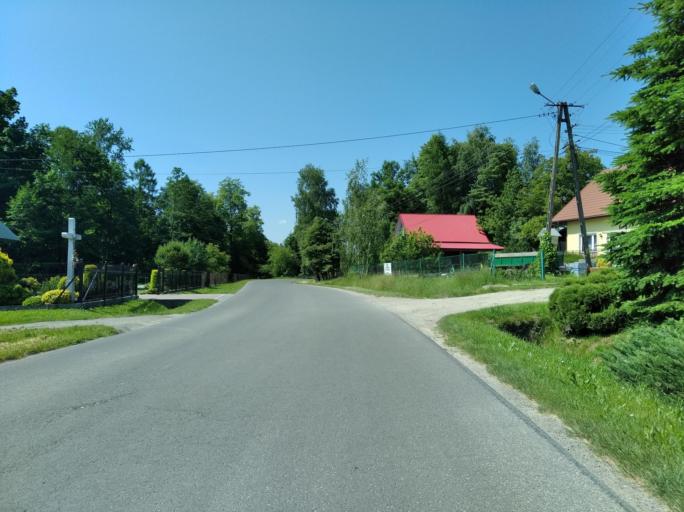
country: PL
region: Subcarpathian Voivodeship
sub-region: Powiat ropczycko-sedziszowski
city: Zagorzyce
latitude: 50.0143
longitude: 21.6729
